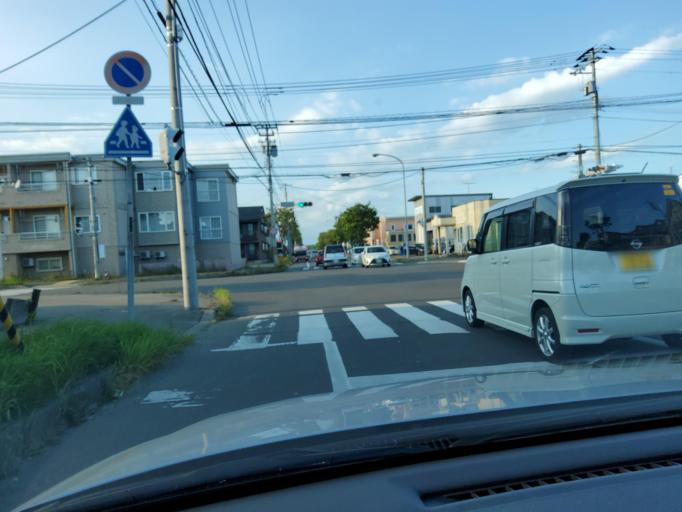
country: JP
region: Hokkaido
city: Obihiro
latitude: 42.9354
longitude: 143.1844
